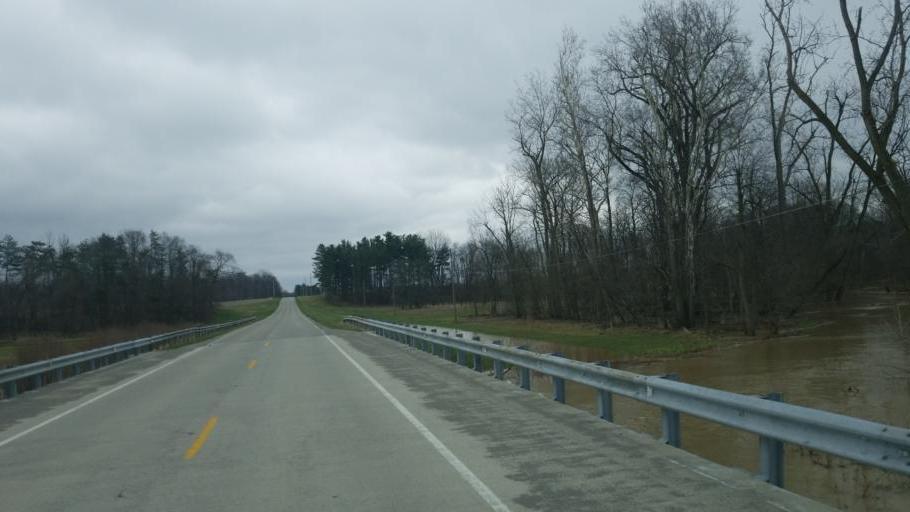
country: US
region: Ohio
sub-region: Wyandot County
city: Upper Sandusky
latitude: 40.8262
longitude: -83.1532
